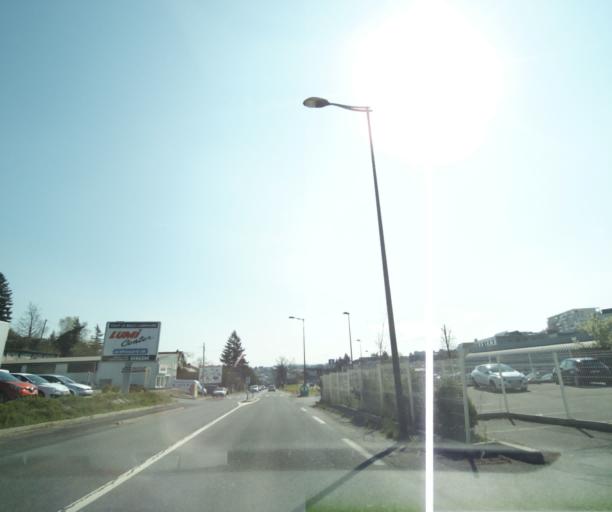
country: FR
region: Midi-Pyrenees
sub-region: Departement de l'Aveyron
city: Olemps
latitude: 44.3636
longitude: 2.5552
